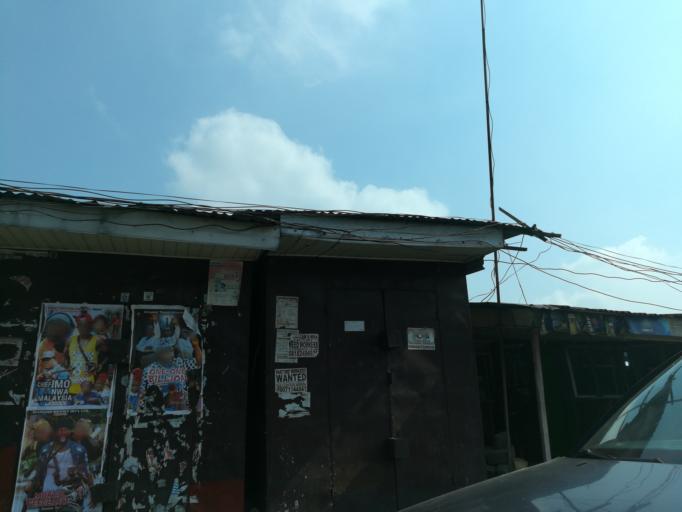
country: NG
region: Rivers
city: Port Harcourt
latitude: 4.8322
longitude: 6.9839
